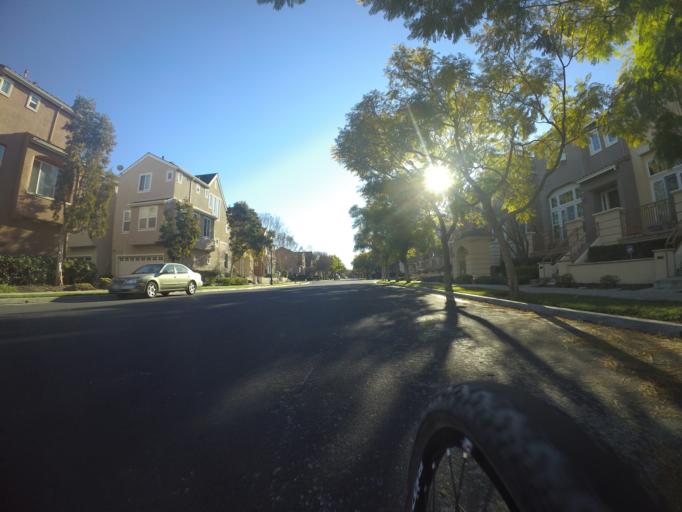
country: US
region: California
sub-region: Santa Clara County
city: Santa Clara
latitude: 37.4003
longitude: -121.9499
